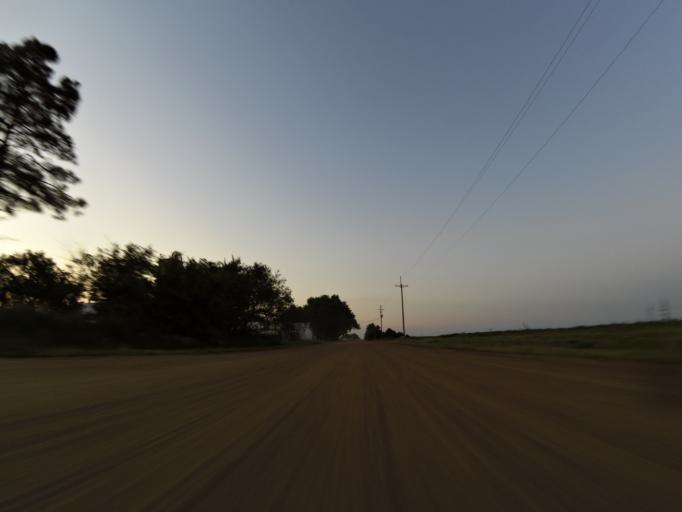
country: US
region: Kansas
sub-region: Reno County
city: South Hutchinson
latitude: 37.9899
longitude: -98.0319
